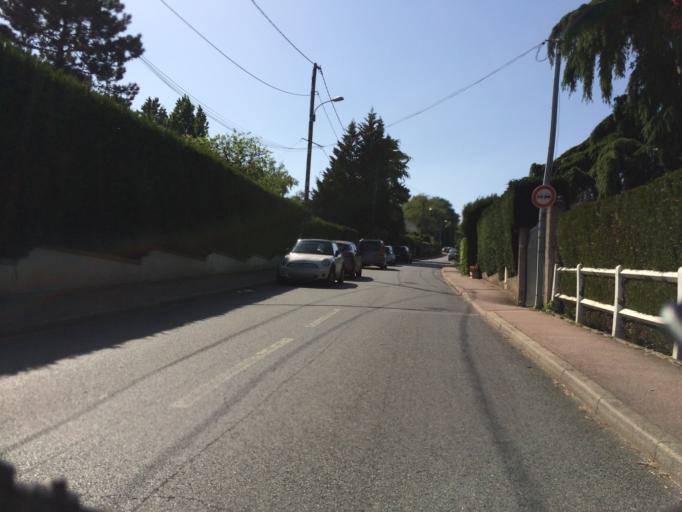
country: FR
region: Ile-de-France
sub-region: Departement de l'Essonne
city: Verrieres-le-Buisson
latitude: 48.7474
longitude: 2.2572
